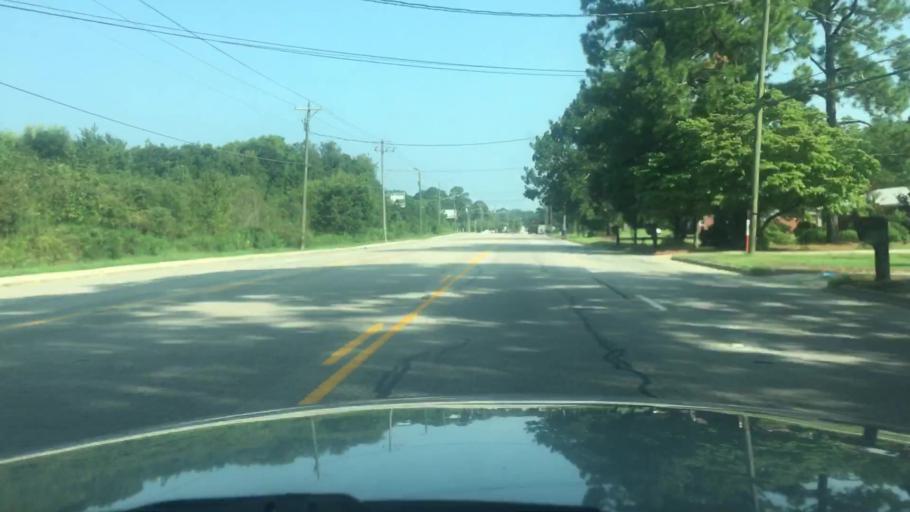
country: US
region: North Carolina
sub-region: Cumberland County
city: Vander
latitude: 35.0216
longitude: -78.8406
